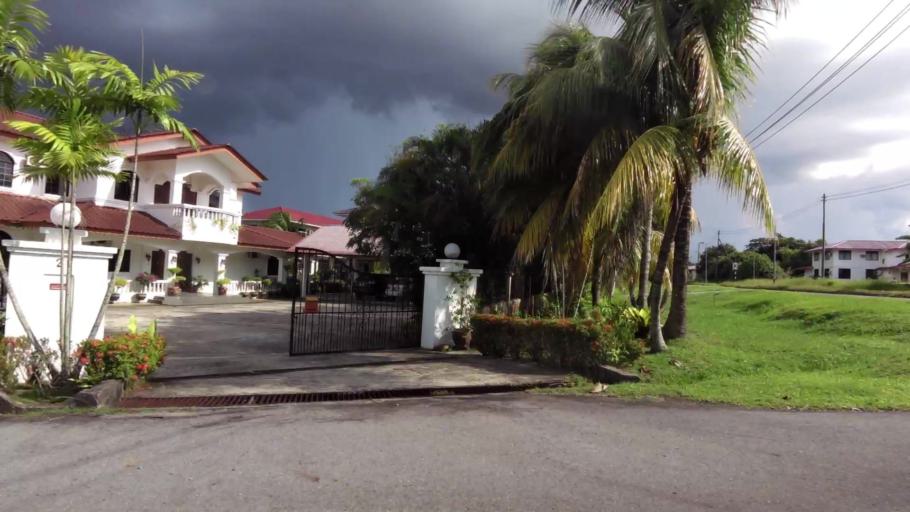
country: BN
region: Brunei and Muara
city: Bandar Seri Begawan
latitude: 4.9604
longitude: 114.9626
